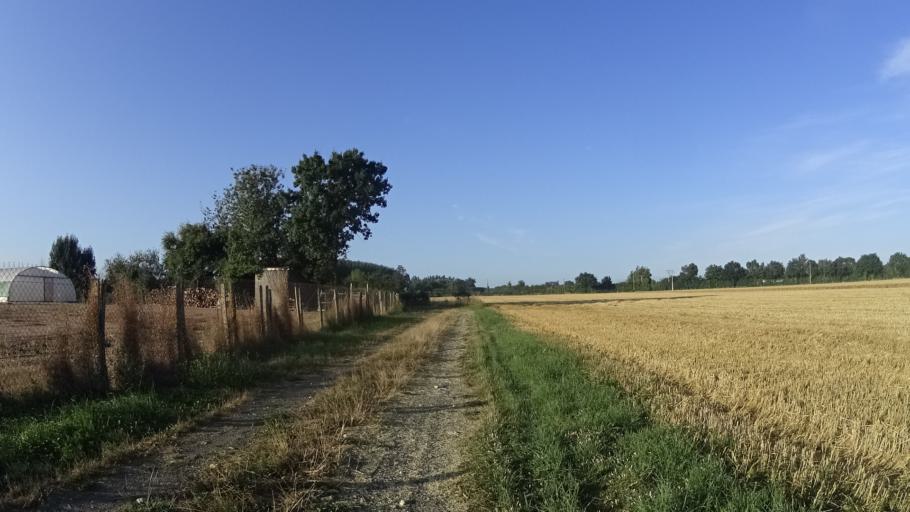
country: FR
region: Pays de la Loire
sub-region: Departement de Maine-et-Loire
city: Vivy
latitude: 47.3116
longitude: -0.0841
